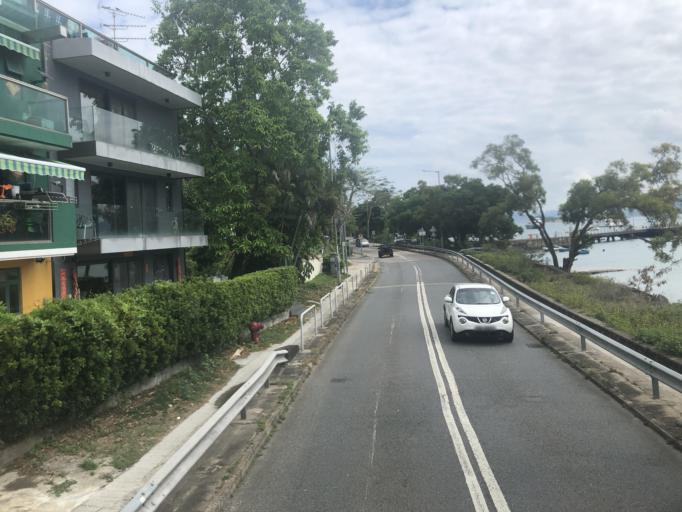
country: HK
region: Sai Kung
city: Sai Kung
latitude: 22.3937
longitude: 114.2891
